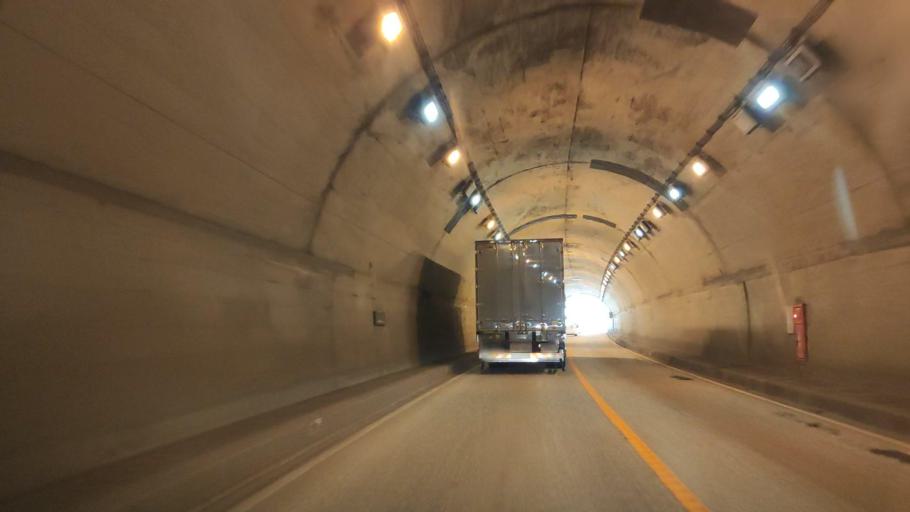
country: JP
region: Aomori
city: Aomori Shi
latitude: 40.7825
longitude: 141.0589
